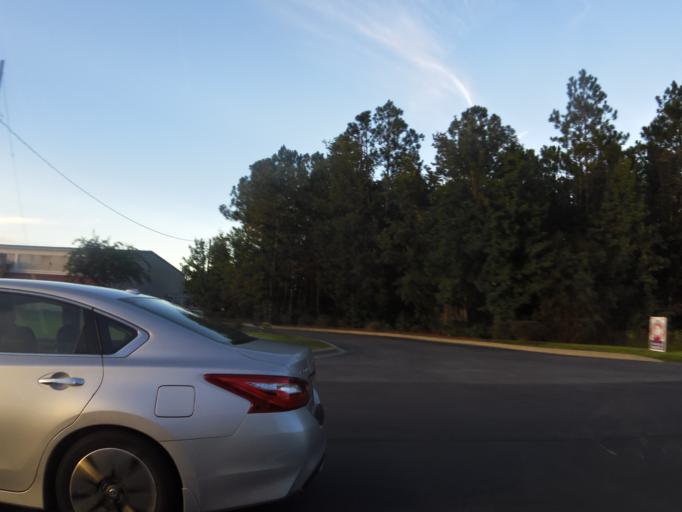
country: US
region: Georgia
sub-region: Camden County
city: Kingsland
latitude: 30.7953
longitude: -81.6704
